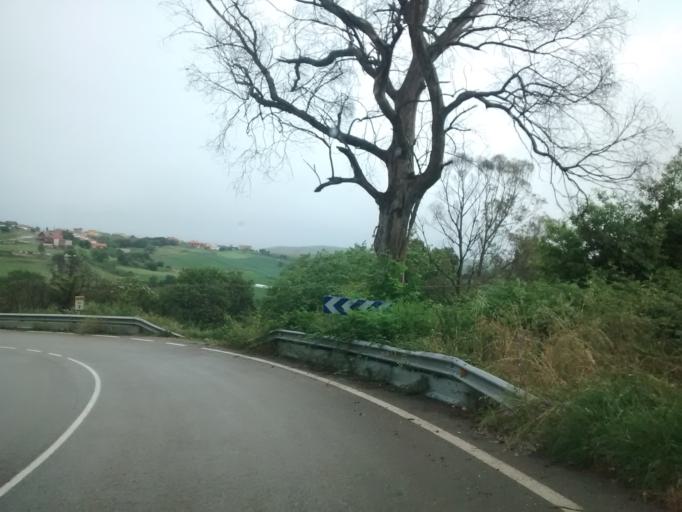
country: ES
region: Cantabria
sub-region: Provincia de Cantabria
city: Santillana
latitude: 43.4101
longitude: -4.0991
